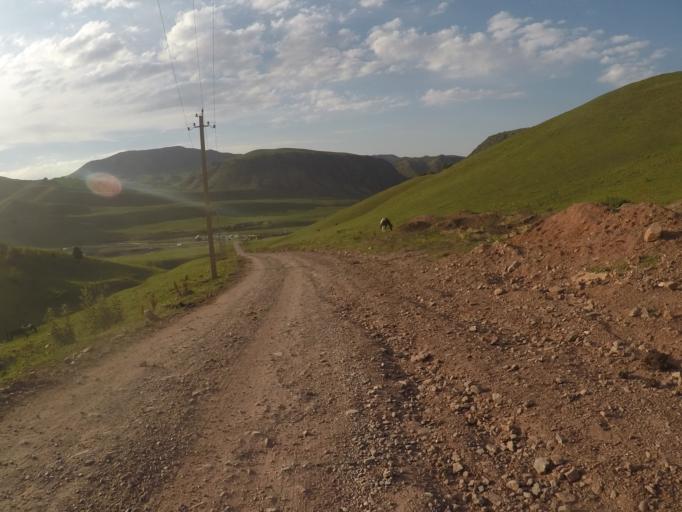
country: KG
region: Chuy
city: Bishkek
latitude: 42.6312
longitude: 74.6184
